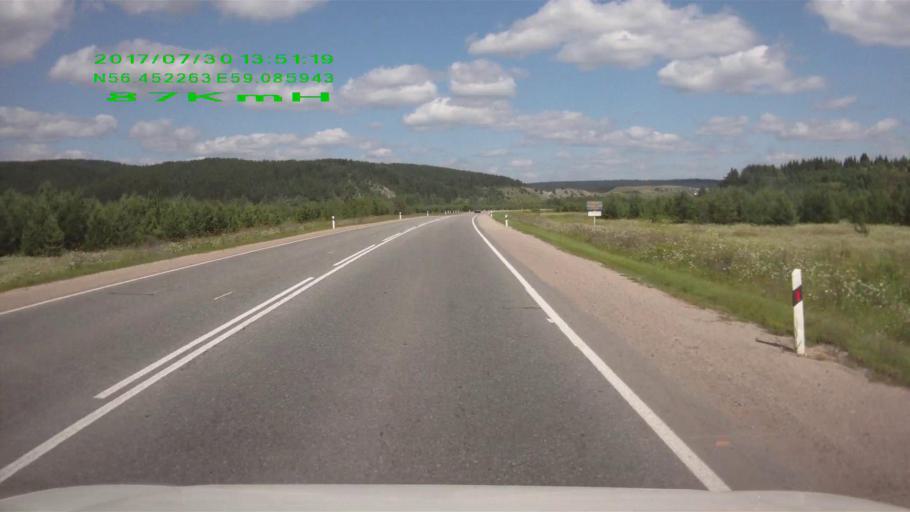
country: RU
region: Sverdlovsk
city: Mikhaylovsk
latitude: 56.4527
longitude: 59.0865
